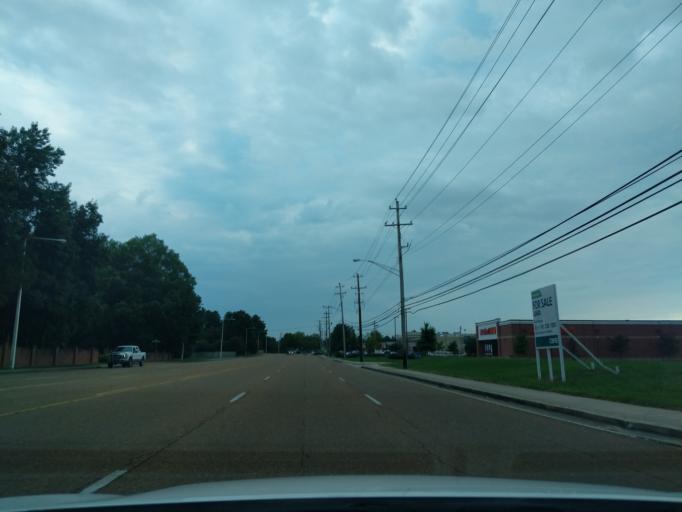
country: US
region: Tennessee
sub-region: Shelby County
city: Germantown
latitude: 35.0742
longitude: -89.8425
